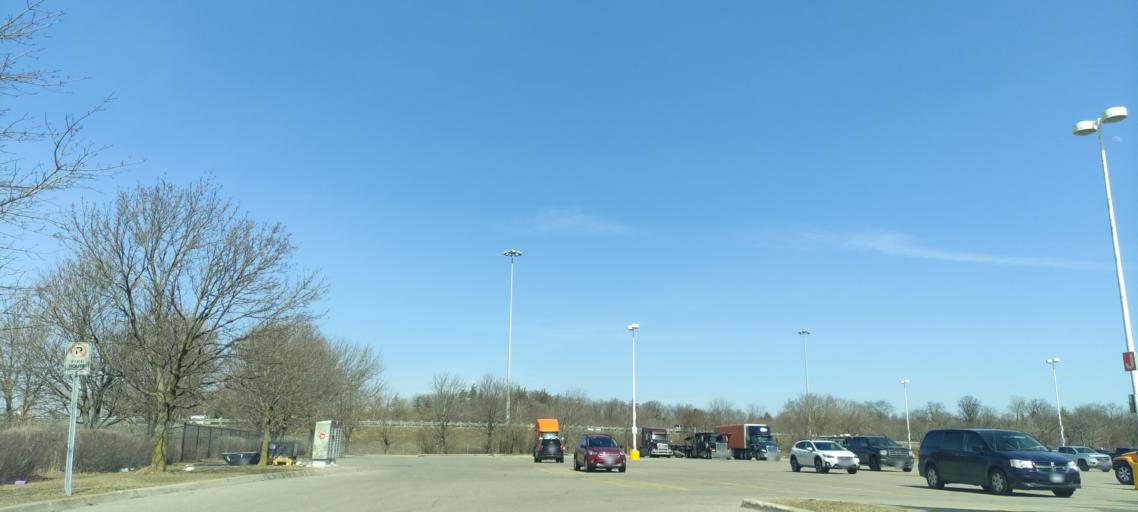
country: CA
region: Ontario
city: Cambridge
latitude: 43.4081
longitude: -80.3911
